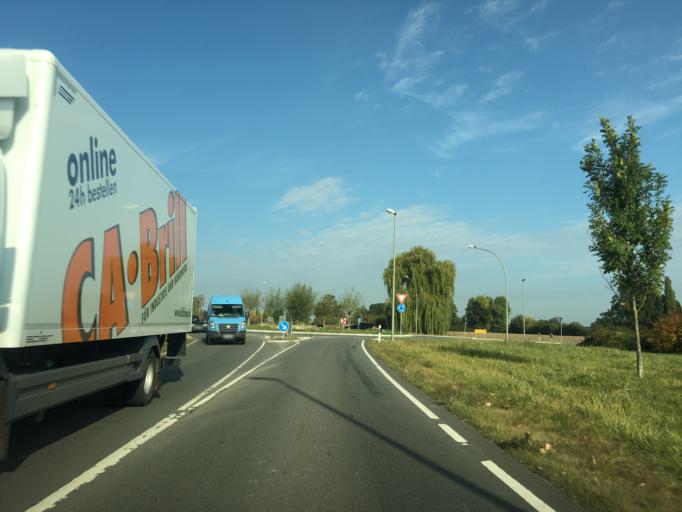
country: DE
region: North Rhine-Westphalia
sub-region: Regierungsbezirk Munster
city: Altenberge
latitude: 52.0513
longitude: 7.4863
